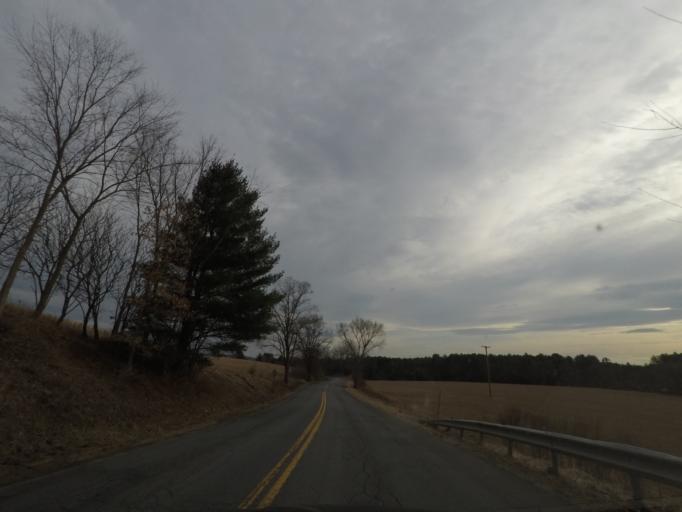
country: US
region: New York
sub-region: Rensselaer County
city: Hoosick Falls
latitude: 42.8712
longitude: -73.4503
